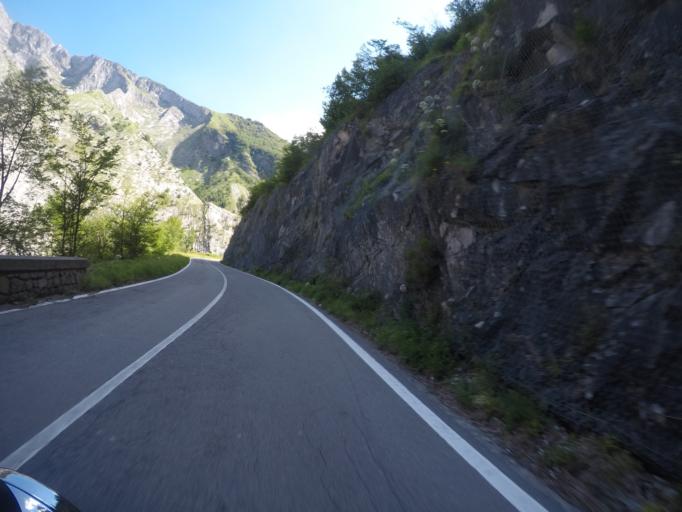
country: IT
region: Tuscany
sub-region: Provincia di Lucca
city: Fontana delle Monache
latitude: 44.0610
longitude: 10.2840
